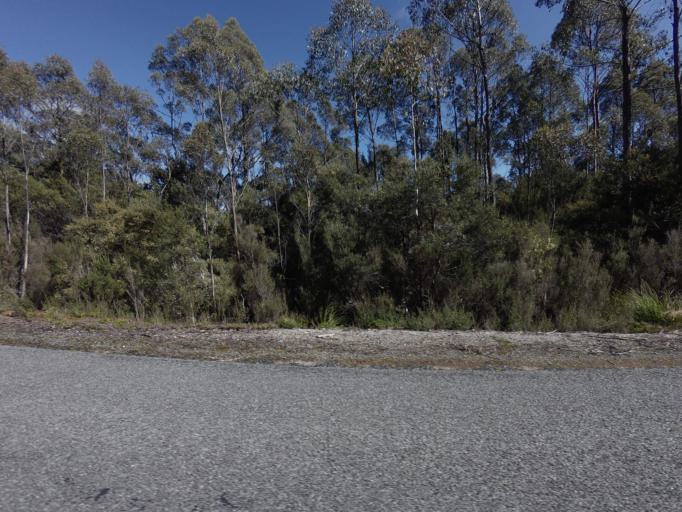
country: AU
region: Tasmania
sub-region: Derwent Valley
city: New Norfolk
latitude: -42.7562
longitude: 146.4091
